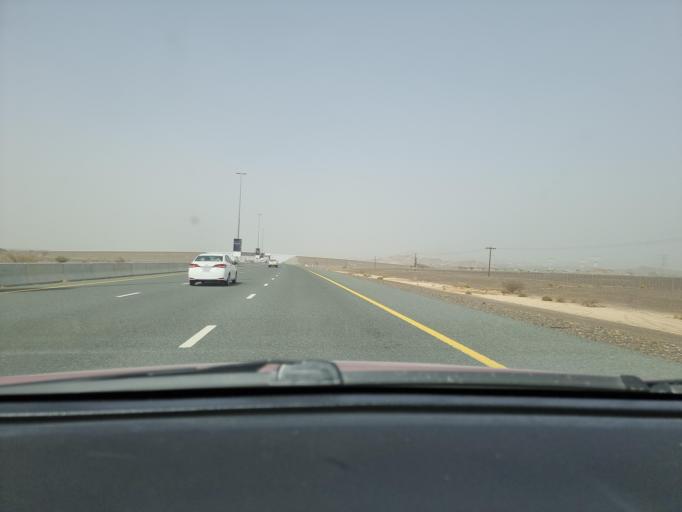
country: AE
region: Ash Shariqah
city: Adh Dhayd
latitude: 25.1412
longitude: 55.9906
